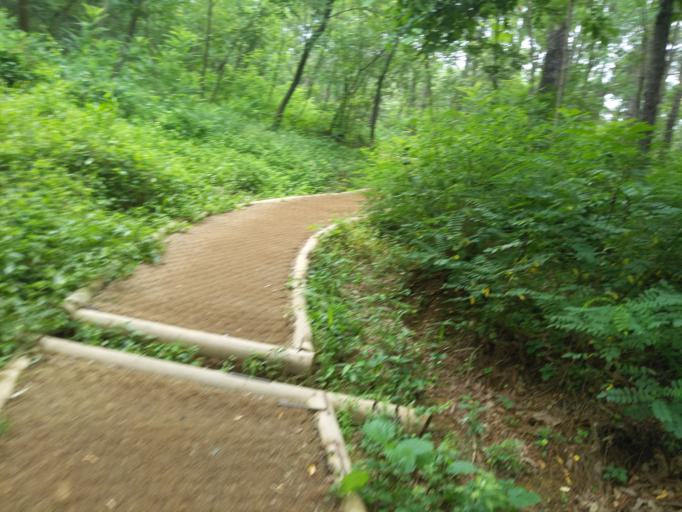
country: KR
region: Daegu
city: Hwawon
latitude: 35.7935
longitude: 128.5259
